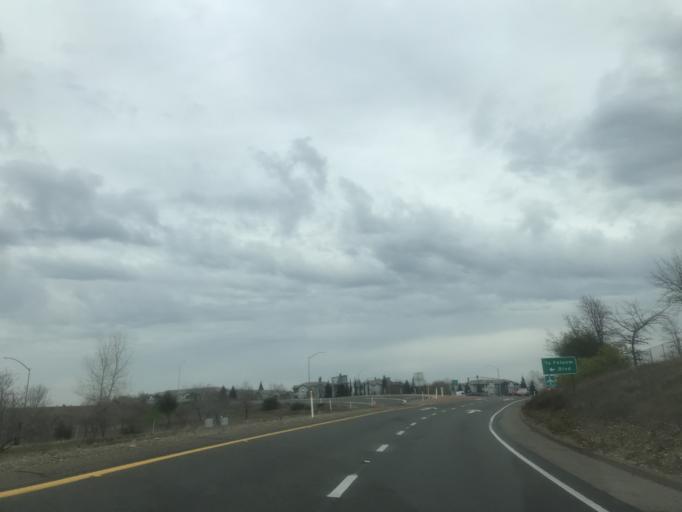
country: US
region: California
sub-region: Sacramento County
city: Rancho Cordova
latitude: 38.5773
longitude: -121.3092
